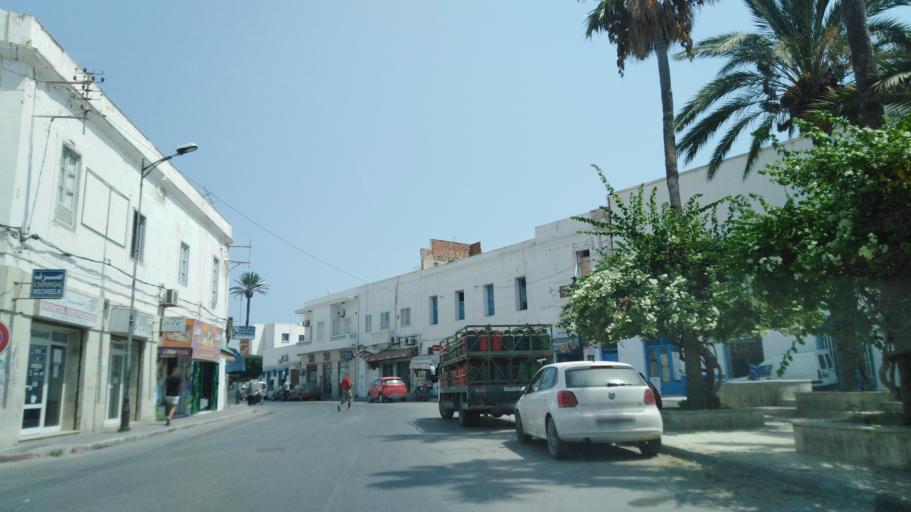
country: TN
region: Al Mahdiyah
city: Mahdia
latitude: 35.5042
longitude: 11.0664
